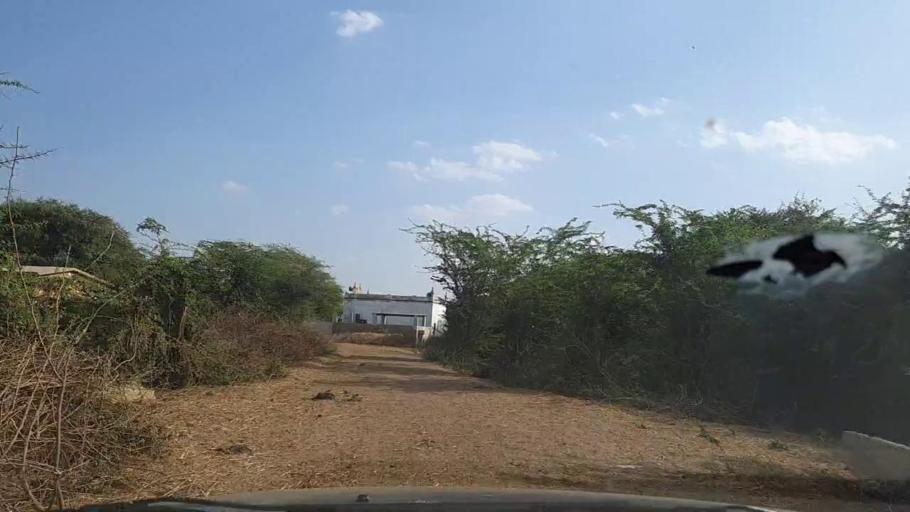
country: PK
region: Sindh
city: Daro Mehar
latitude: 24.8325
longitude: 68.0977
